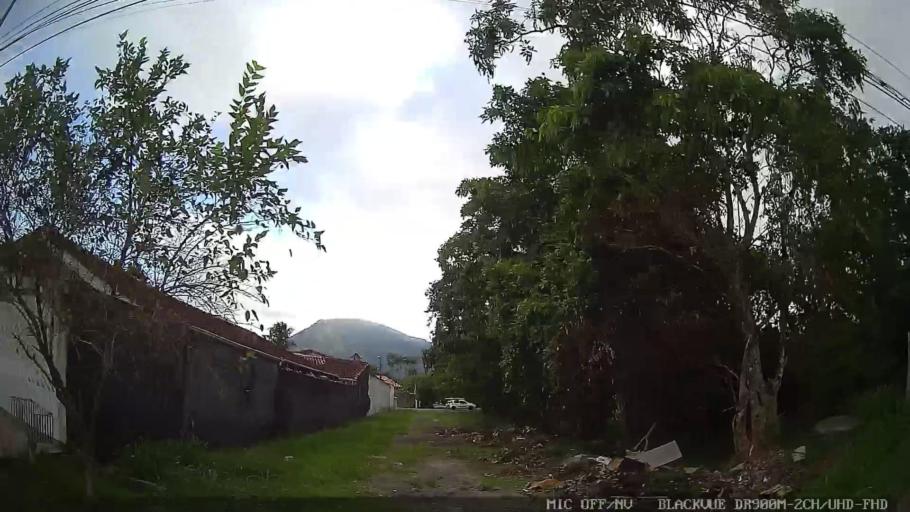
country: BR
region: Sao Paulo
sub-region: Peruibe
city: Peruibe
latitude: -24.3147
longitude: -46.9978
